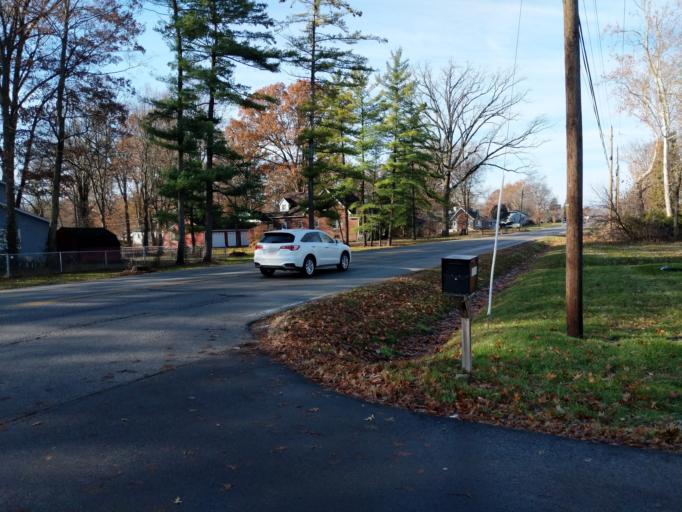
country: US
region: Indiana
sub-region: Marion County
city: Warren Park
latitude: 39.7821
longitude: -86.0118
